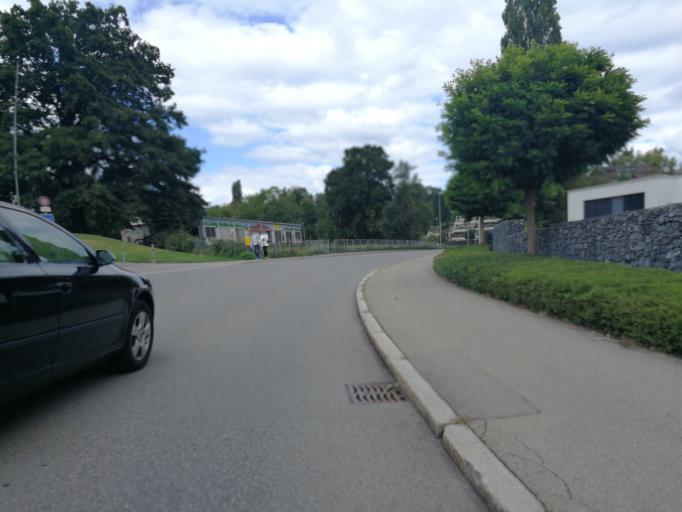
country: CH
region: Zurich
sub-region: Bezirk Meilen
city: Uerikon
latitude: 47.2375
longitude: 8.7548
